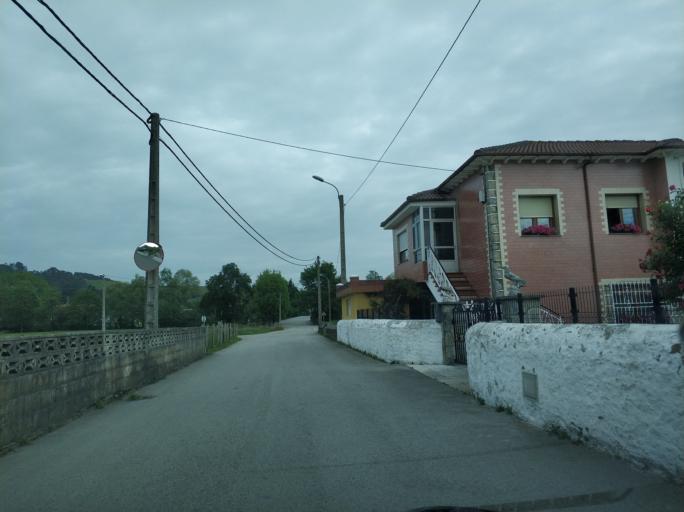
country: ES
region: Cantabria
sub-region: Provincia de Cantabria
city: Santa Maria de Cayon
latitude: 43.3182
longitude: -3.8560
